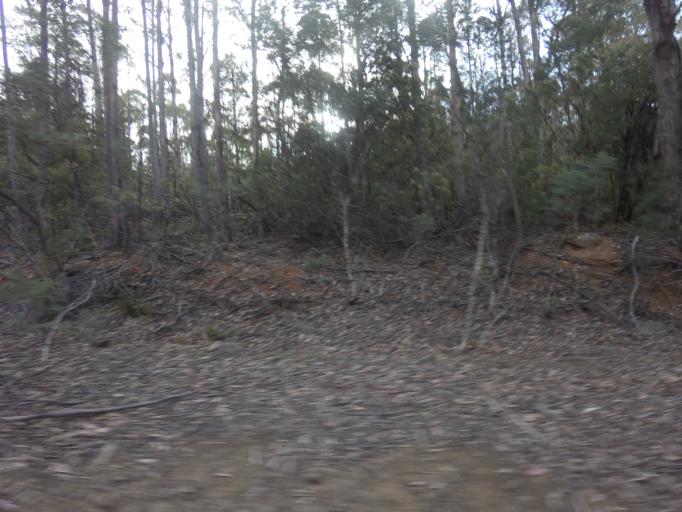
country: AU
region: Tasmania
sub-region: Break O'Day
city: St Helens
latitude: -41.8434
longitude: 148.0620
